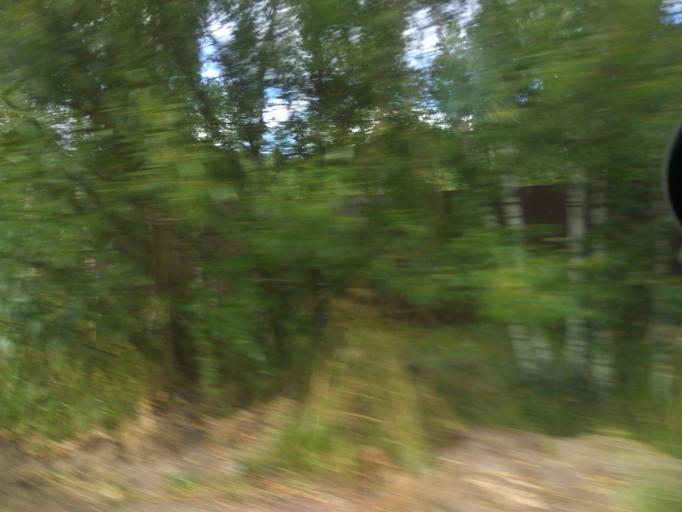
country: RU
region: Moskovskaya
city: Bronnitsy
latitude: 55.4667
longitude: 38.2804
